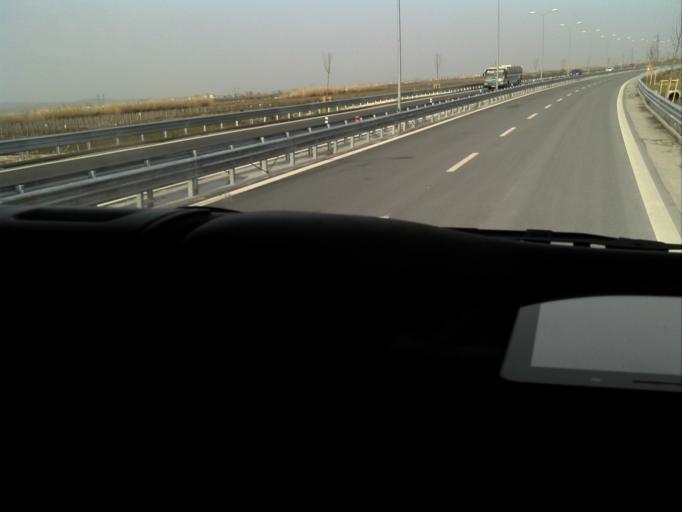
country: AL
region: Tirane
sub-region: Rrethi i Kavajes
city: Gose e Madhe
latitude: 41.0913
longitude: 19.6096
